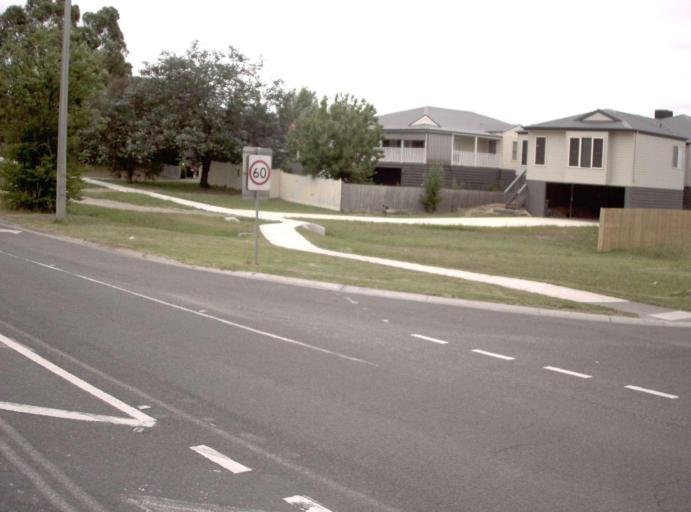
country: AU
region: Victoria
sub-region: Yarra Ranges
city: Yarra Glen
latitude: -37.6564
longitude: 145.3748
